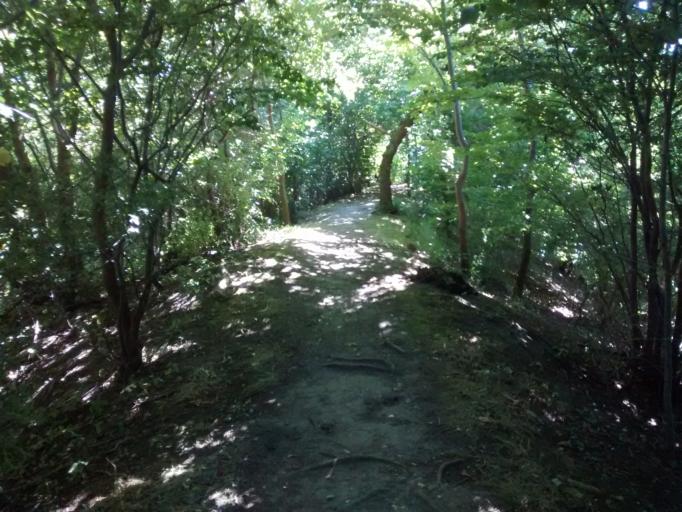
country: DK
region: Zealand
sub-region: Soro Kommune
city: Soro
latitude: 55.4521
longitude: 11.5536
